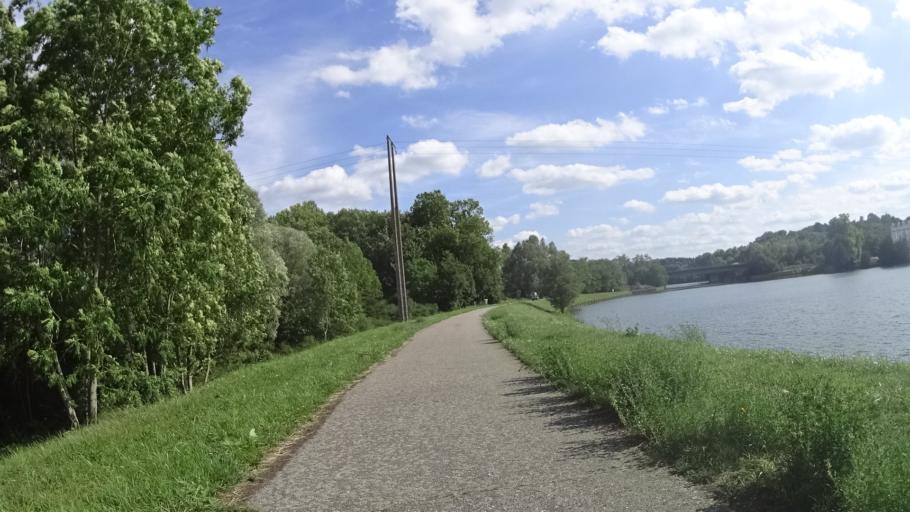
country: FR
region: Lorraine
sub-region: Departement de Meurthe-et-Moselle
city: Dommartin-les-Toul
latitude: 48.6597
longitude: 5.8966
